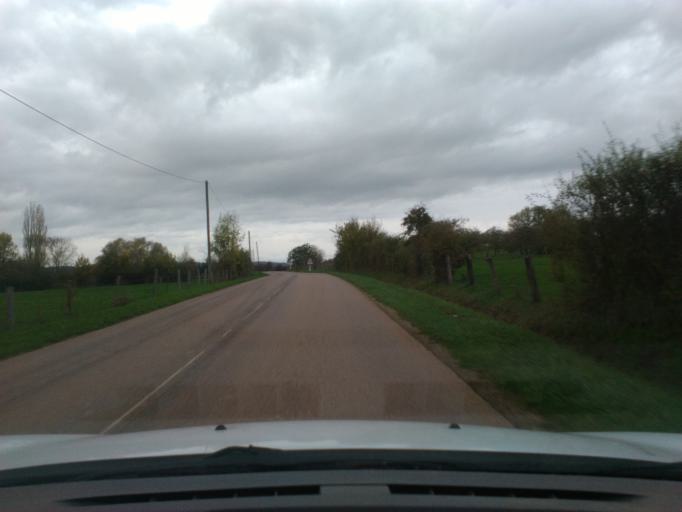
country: FR
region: Lorraine
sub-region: Departement des Vosges
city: Mirecourt
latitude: 48.3506
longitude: 6.0918
